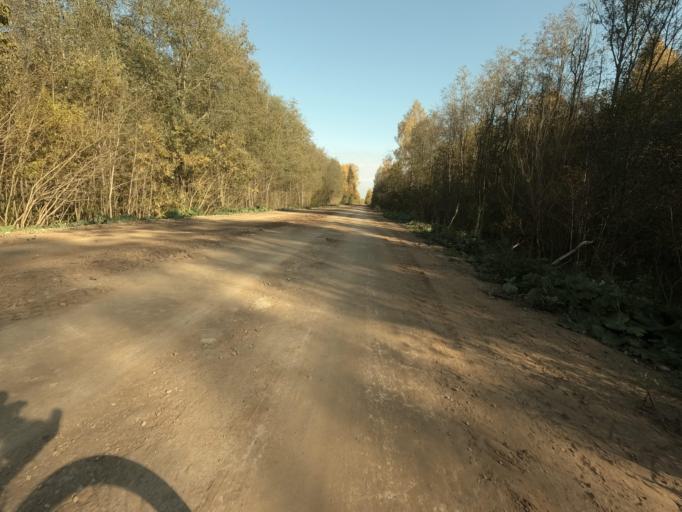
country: RU
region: Novgorod
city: Batetskiy
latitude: 58.8272
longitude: 30.7106
